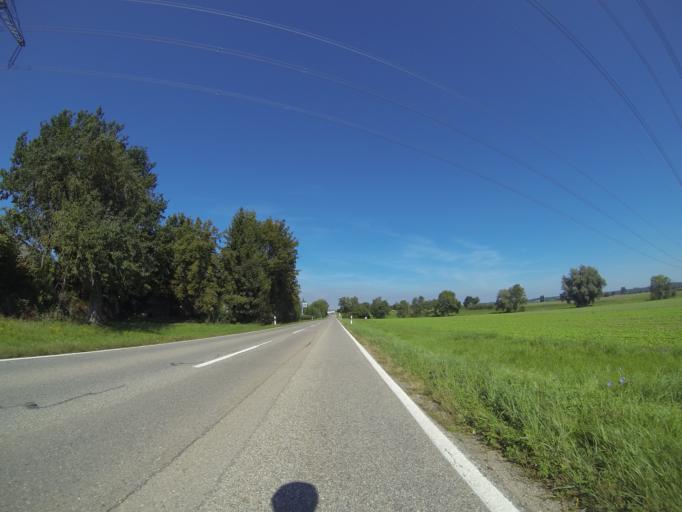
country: DE
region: Baden-Wuerttemberg
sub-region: Tuebingen Region
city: Achstetten
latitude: 48.2954
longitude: 9.9067
